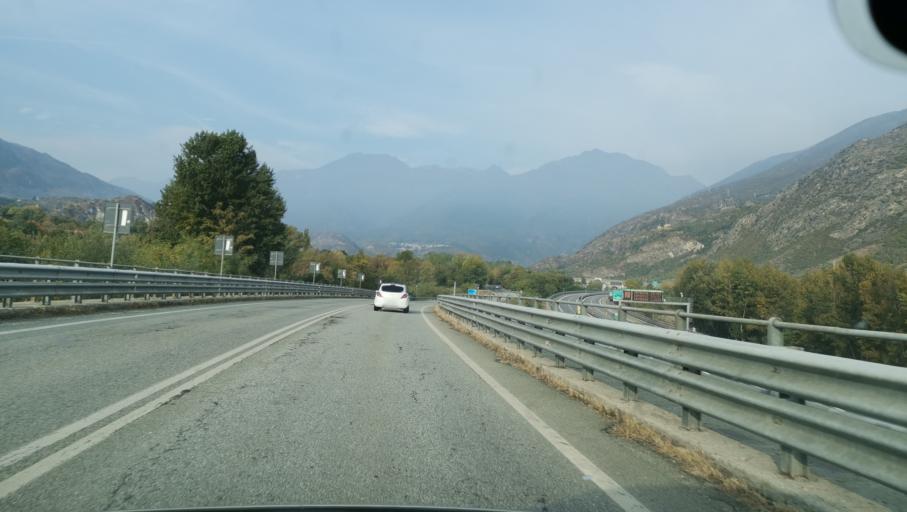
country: IT
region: Piedmont
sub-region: Provincia di Torino
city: Mattie
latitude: 45.1322
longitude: 7.1025
